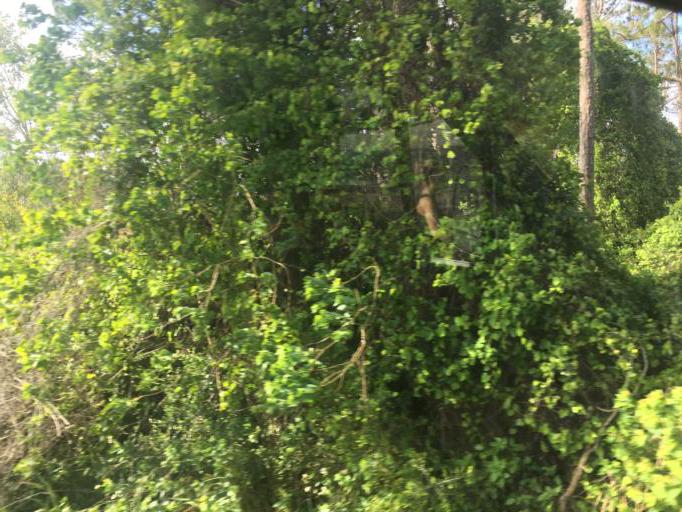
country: US
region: Florida
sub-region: Bay County
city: Panama City Beach
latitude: 30.2130
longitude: -85.8441
